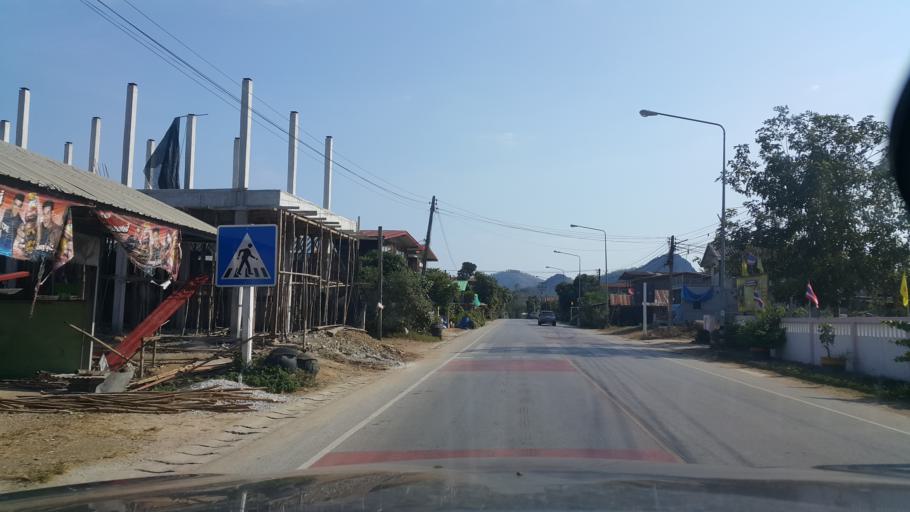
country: LA
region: Vientiane
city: Muang Sanakham
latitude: 17.9063
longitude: 101.7247
